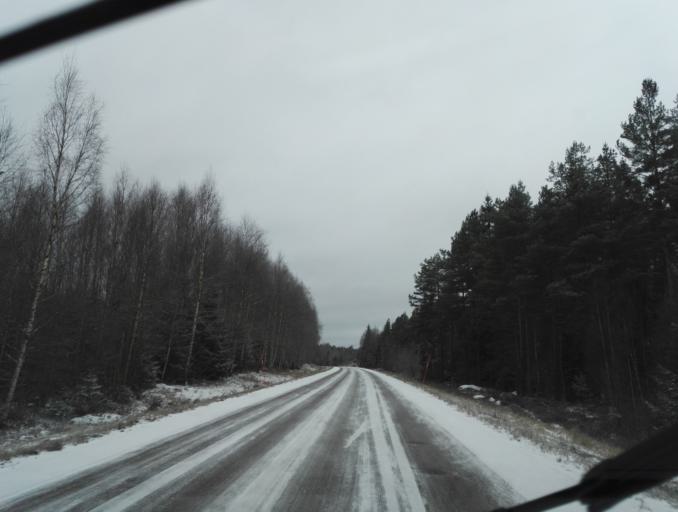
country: SE
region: Kronoberg
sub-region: Lessebo Kommun
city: Lessebo
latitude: 56.7382
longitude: 15.2482
